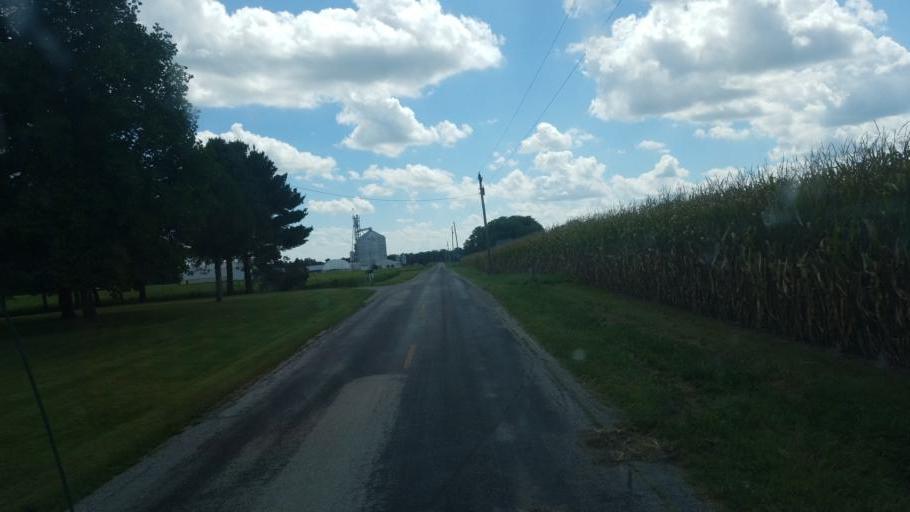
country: US
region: Ohio
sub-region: Marion County
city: Prospect
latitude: 40.4634
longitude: -83.1682
